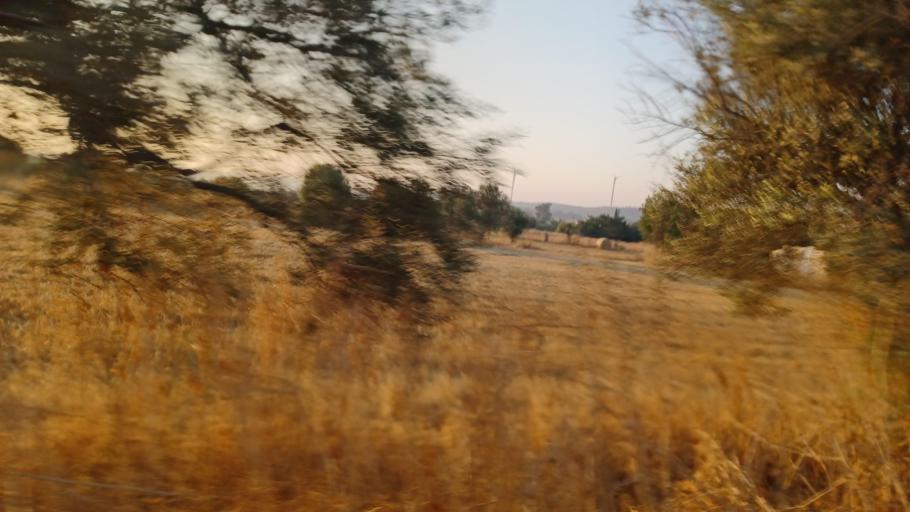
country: CY
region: Larnaka
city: Tersefanou
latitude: 34.8962
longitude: 33.5138
